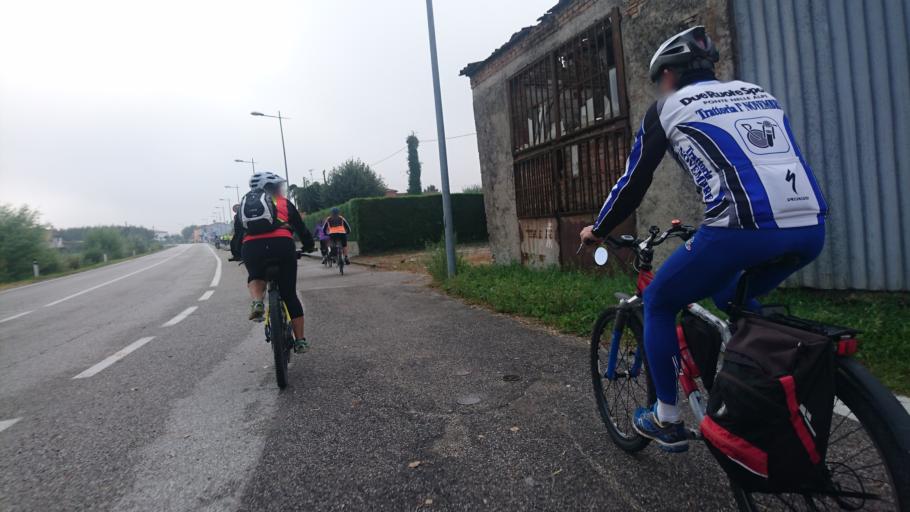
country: IT
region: Veneto
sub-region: Provincia di Padova
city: Pozzonovo
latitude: 45.2098
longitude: 11.7759
